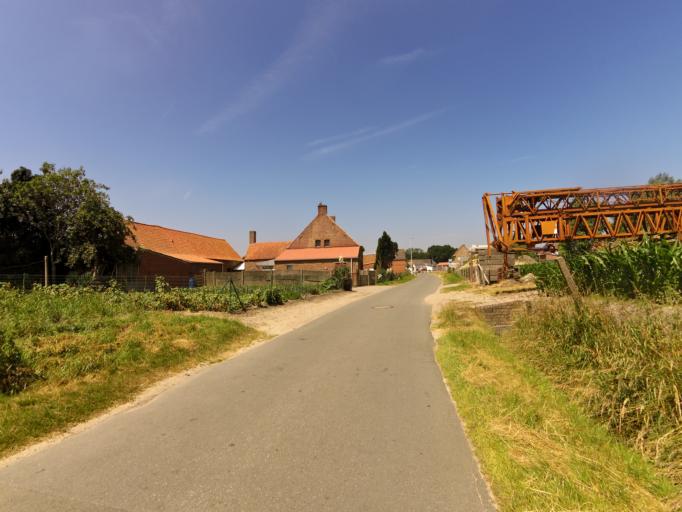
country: BE
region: Flanders
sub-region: Provincie West-Vlaanderen
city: Zedelgem
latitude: 51.1666
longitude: 3.1261
